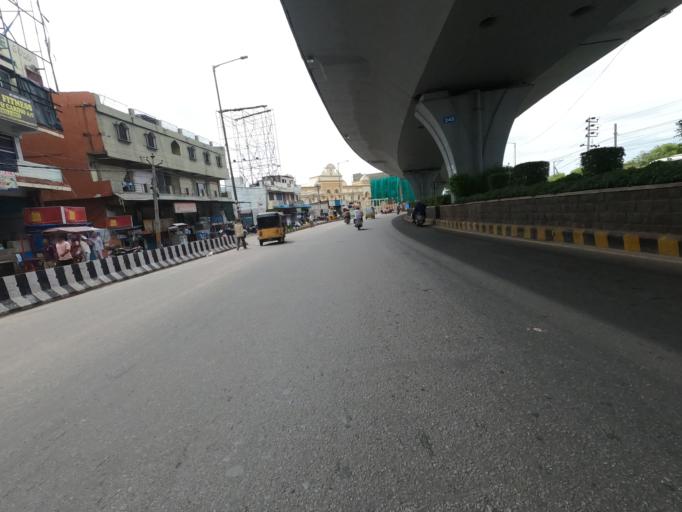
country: IN
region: Telangana
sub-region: Hyderabad
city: Hyderabad
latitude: 17.3419
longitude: 78.4230
